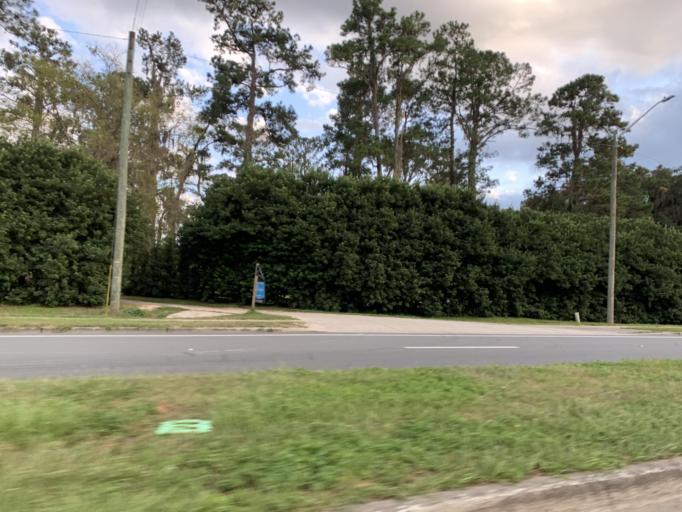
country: US
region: Florida
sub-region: Marion County
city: Ocala
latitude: 29.1507
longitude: -82.1554
